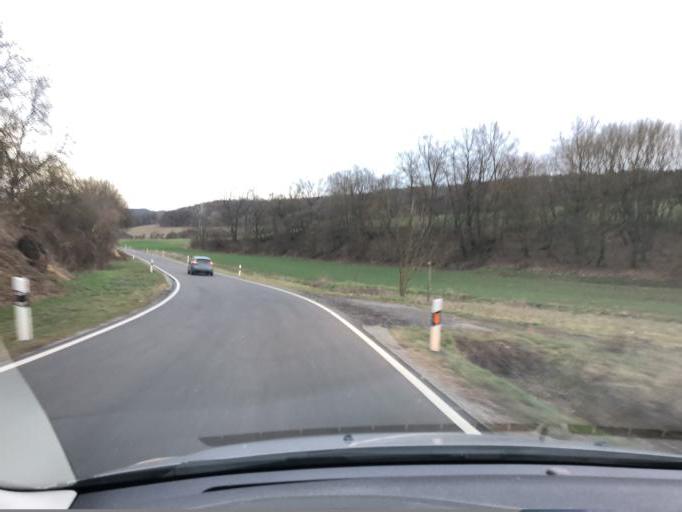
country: DE
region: Saxony-Anhalt
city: Balgstadt
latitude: 51.2062
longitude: 11.7073
